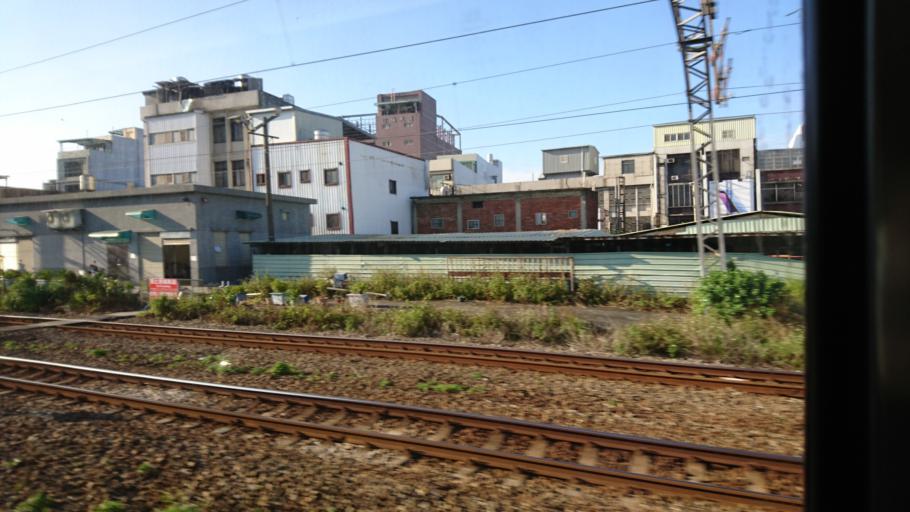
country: TW
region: Taiwan
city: Taoyuan City
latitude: 24.9725
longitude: 121.2591
